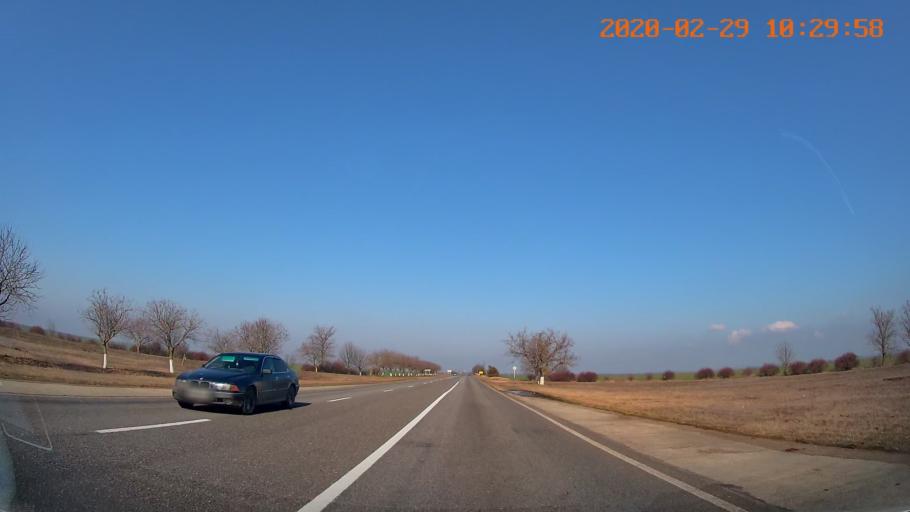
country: MD
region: Telenesti
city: Tiraspolul Nou
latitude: 46.9296
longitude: 29.5804
